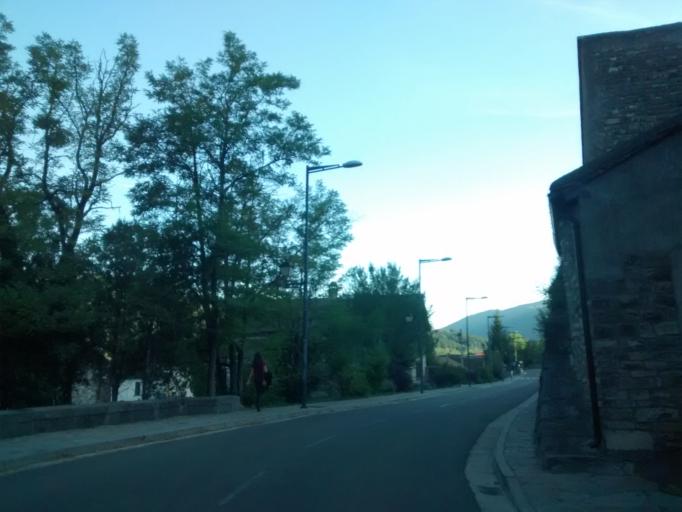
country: ES
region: Aragon
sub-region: Provincia de Huesca
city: Anso
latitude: 42.7380
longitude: -0.7517
